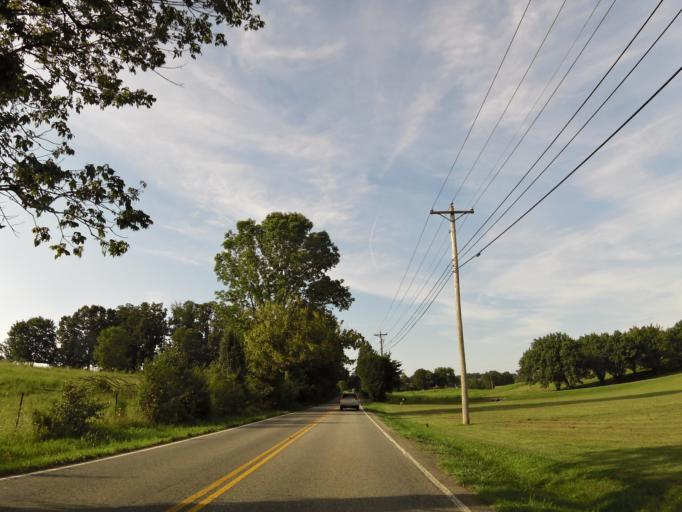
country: US
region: Tennessee
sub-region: Sevier County
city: Seymour
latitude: 35.8409
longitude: -83.7894
